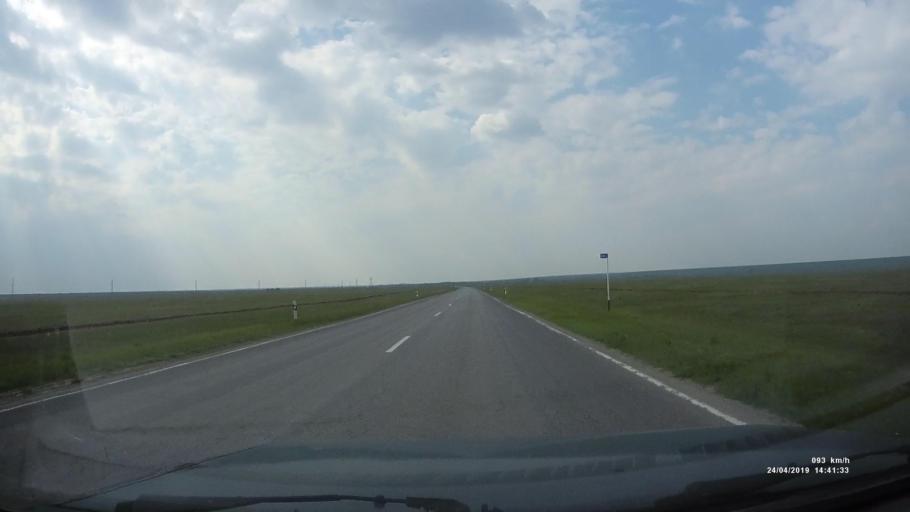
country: RU
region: Rostov
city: Remontnoye
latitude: 46.4460
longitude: 43.8781
